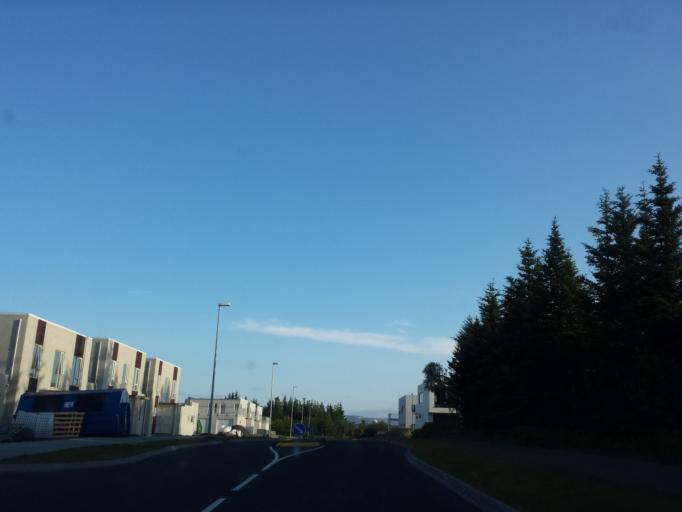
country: IS
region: Capital Region
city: Mosfellsbaer
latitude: 64.0969
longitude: -21.7778
